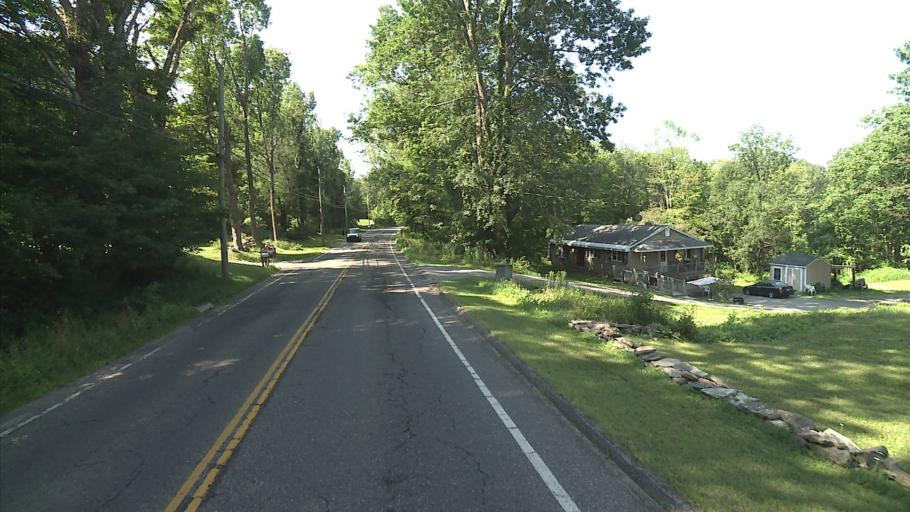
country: US
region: Connecticut
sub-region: Litchfield County
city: Winsted
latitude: 41.8998
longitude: -73.0634
